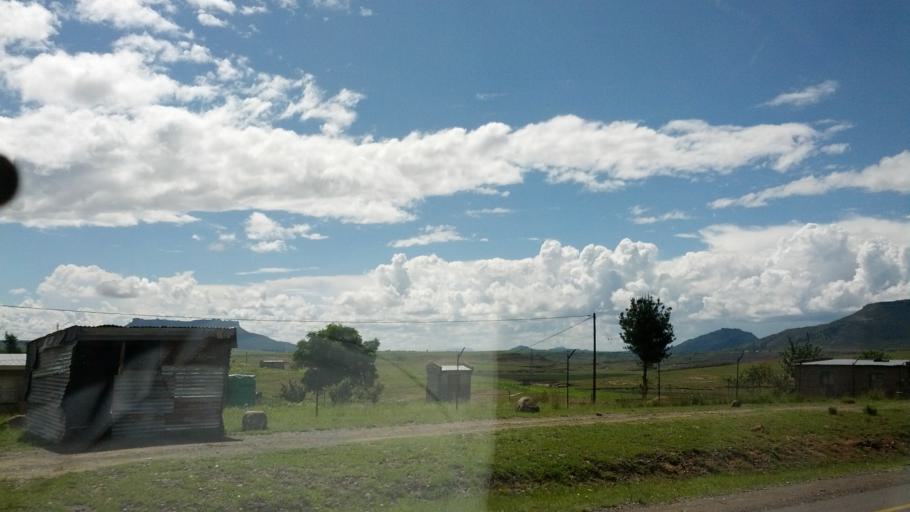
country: LS
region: Mafeteng
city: Mafeteng
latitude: -29.6631
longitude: 27.4543
